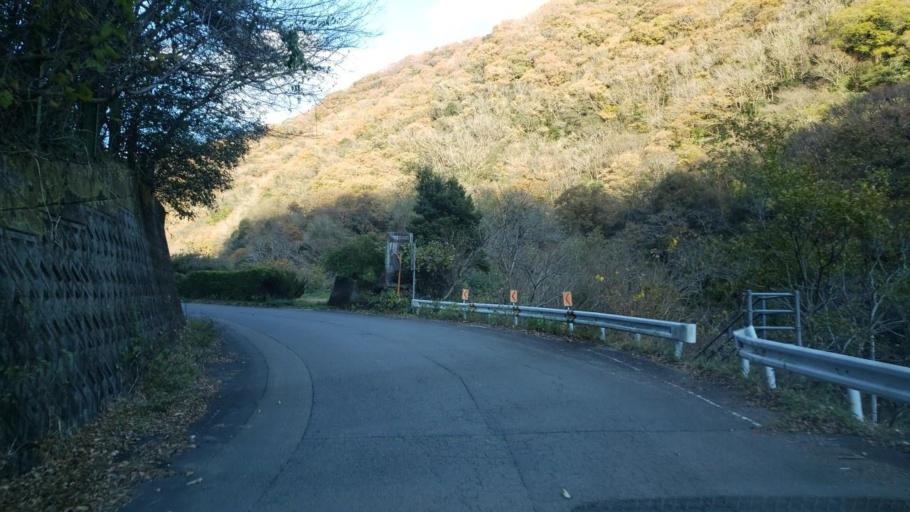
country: JP
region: Tokushima
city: Wakimachi
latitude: 34.0828
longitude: 134.0726
